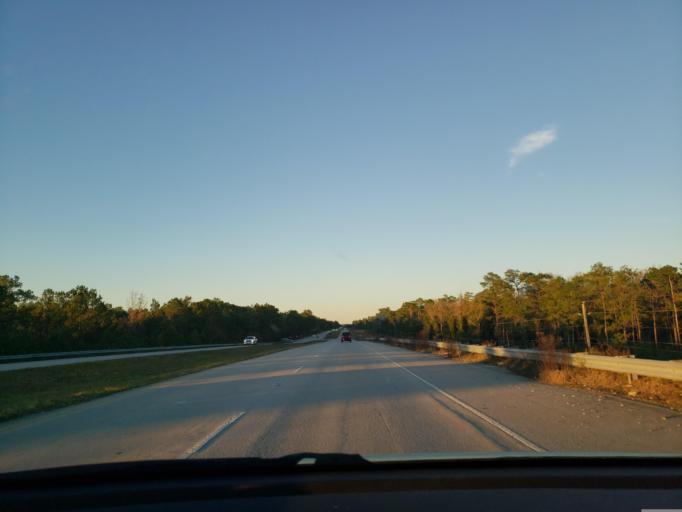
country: US
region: North Carolina
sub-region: Onslow County
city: Sneads Ferry
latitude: 34.6369
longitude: -77.4796
